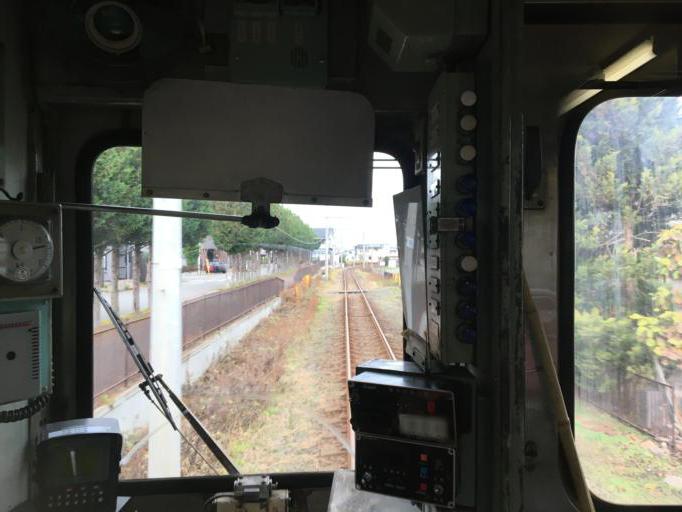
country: JP
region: Aomori
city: Hirosaki
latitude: 40.5725
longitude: 140.4748
